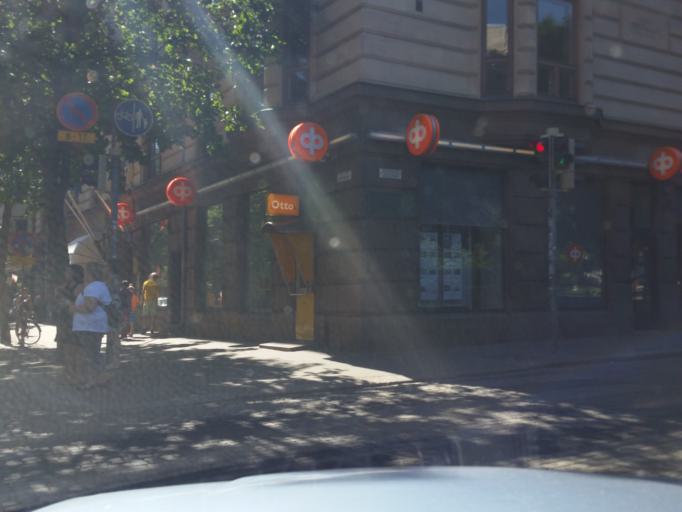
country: FI
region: Uusimaa
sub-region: Helsinki
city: Helsinki
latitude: 60.1652
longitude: 24.9393
